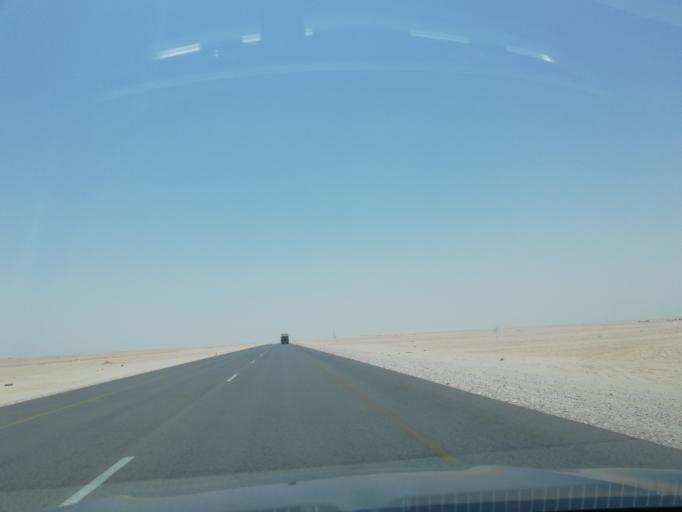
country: OM
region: Al Wusta
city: Hayma'
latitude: 20.2682
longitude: 56.5865
